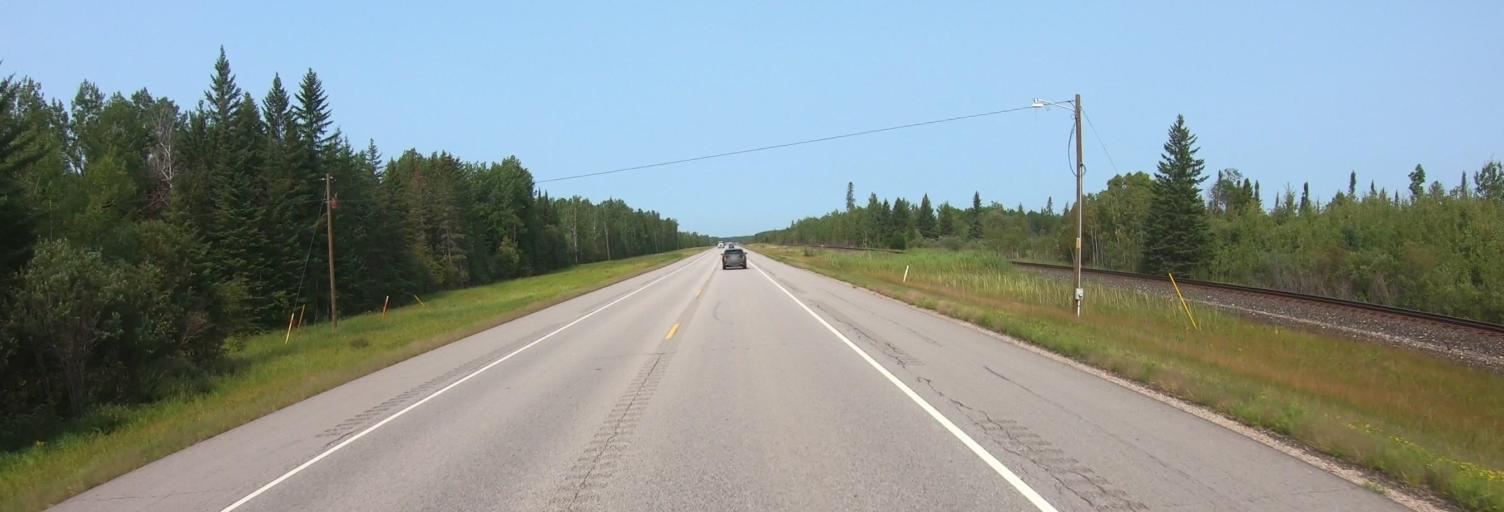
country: CA
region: Ontario
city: Fort Frances
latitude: 48.4677
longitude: -93.2963
